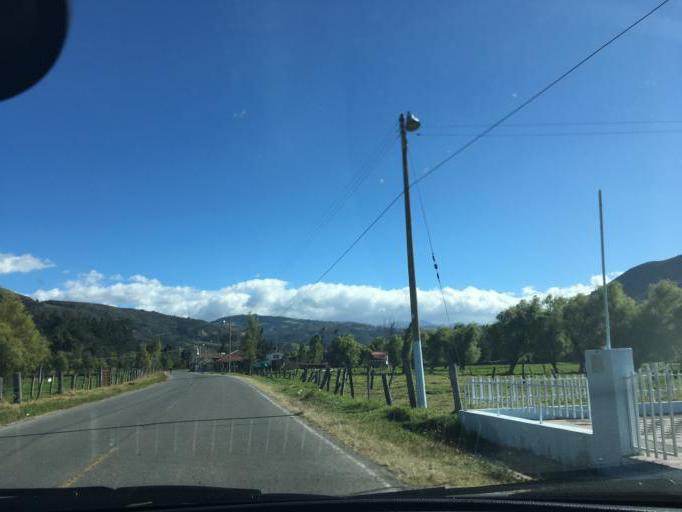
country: CO
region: Boyaca
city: Firavitoba
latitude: 5.6223
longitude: -72.9822
